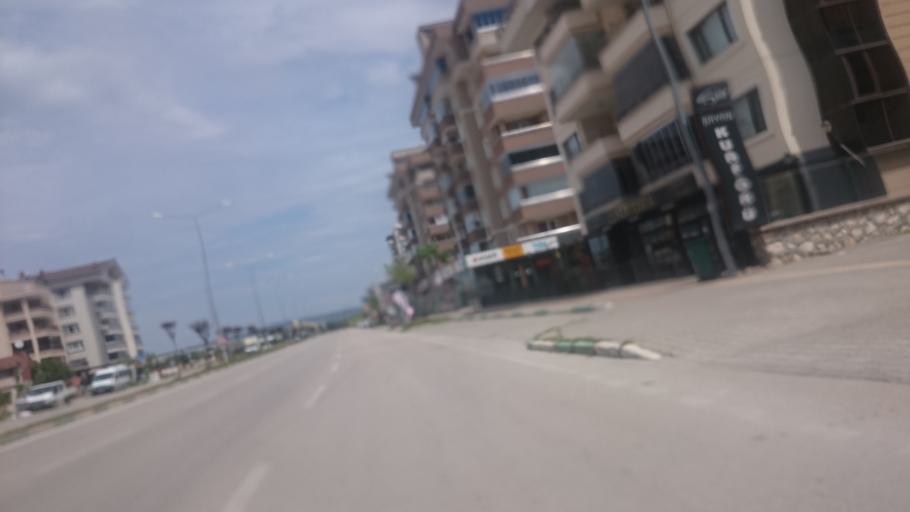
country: TR
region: Bursa
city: Cali
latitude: 40.2294
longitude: 28.9161
